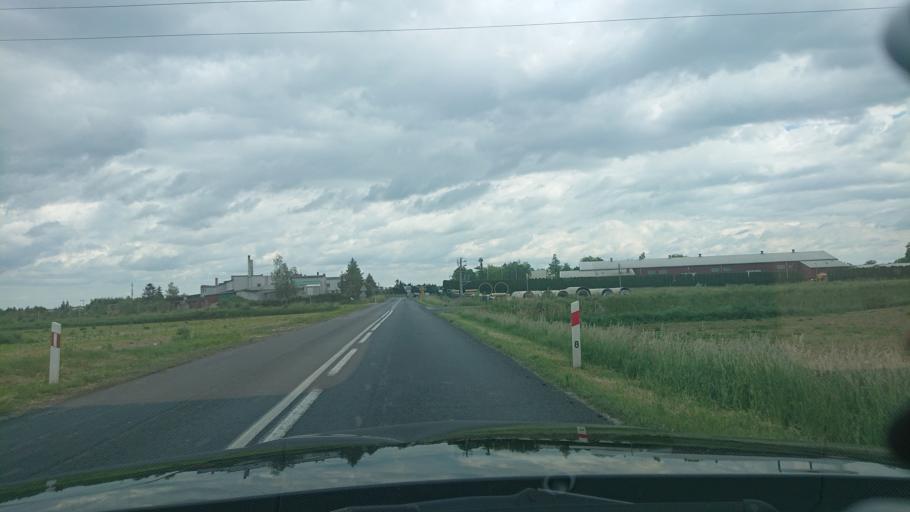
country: PL
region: Greater Poland Voivodeship
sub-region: Powiat gnieznienski
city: Gniezno
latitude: 52.5350
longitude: 17.5428
